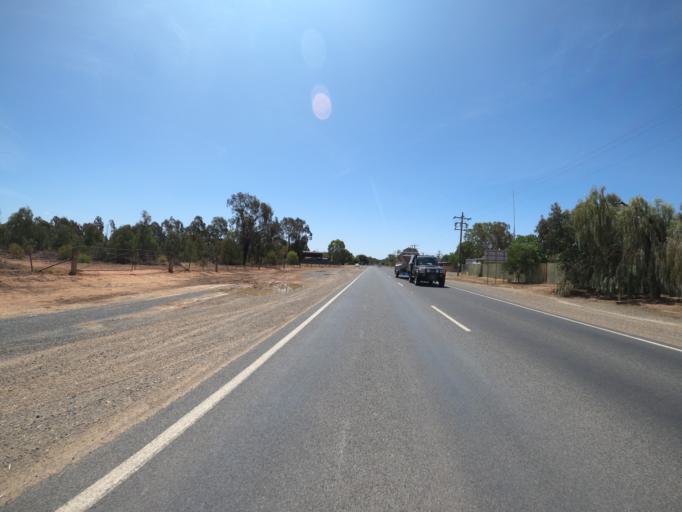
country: AU
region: Victoria
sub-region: Moira
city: Yarrawonga
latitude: -36.0225
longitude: 145.9955
